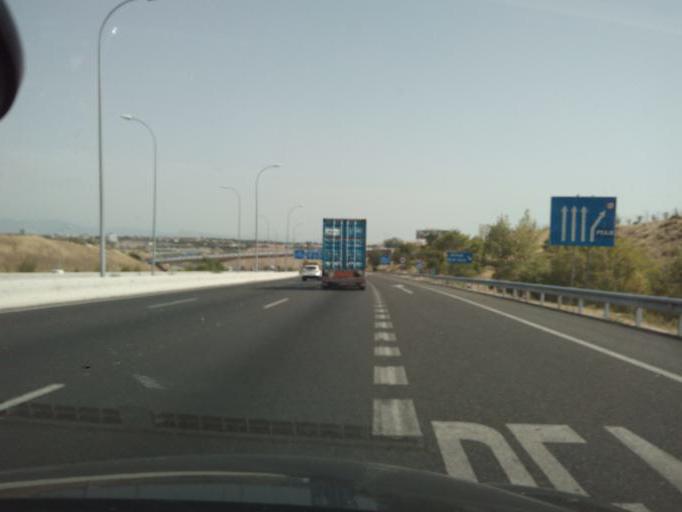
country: ES
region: Madrid
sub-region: Provincia de Madrid
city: Hortaleza
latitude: 40.4869
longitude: -3.6440
